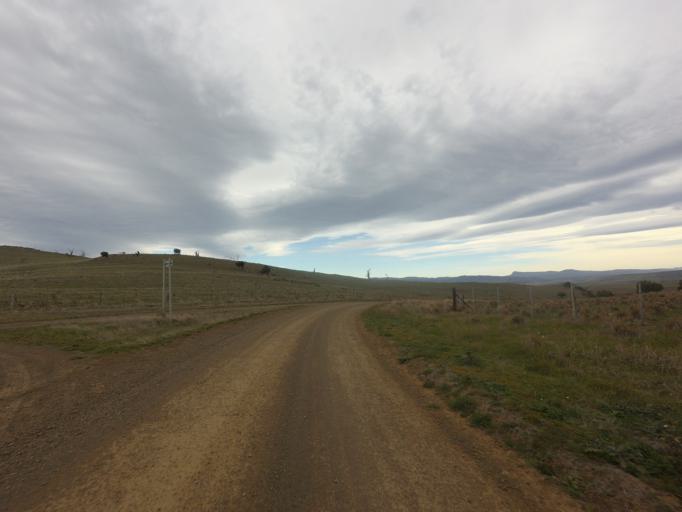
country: AU
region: Tasmania
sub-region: Derwent Valley
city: New Norfolk
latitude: -42.4357
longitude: 146.8143
